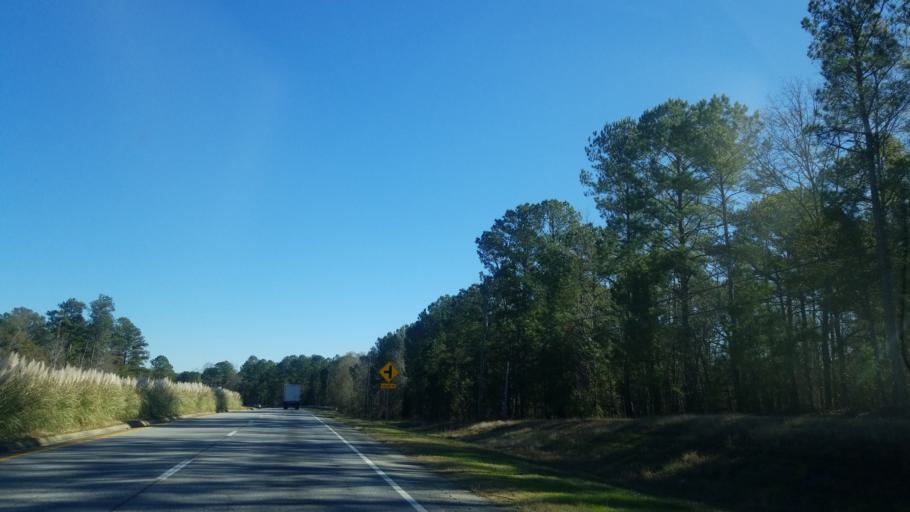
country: US
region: Georgia
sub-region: Muscogee County
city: Columbus
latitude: 32.5407
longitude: -84.8213
